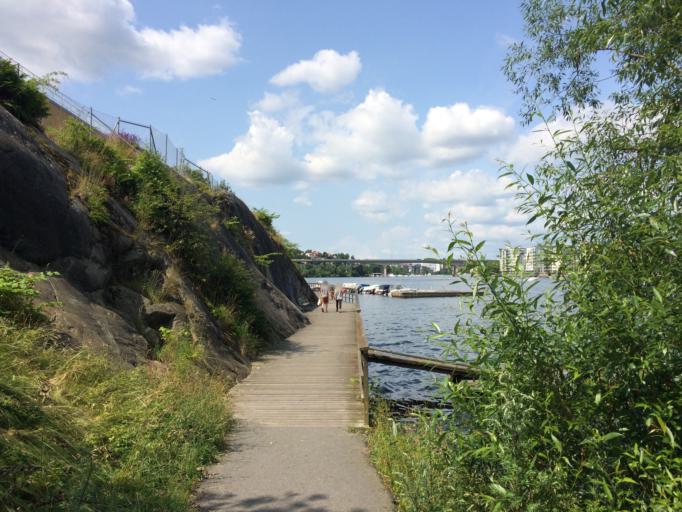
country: SE
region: Stockholm
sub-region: Solna Kommun
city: Solna
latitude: 59.3181
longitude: 18.0093
